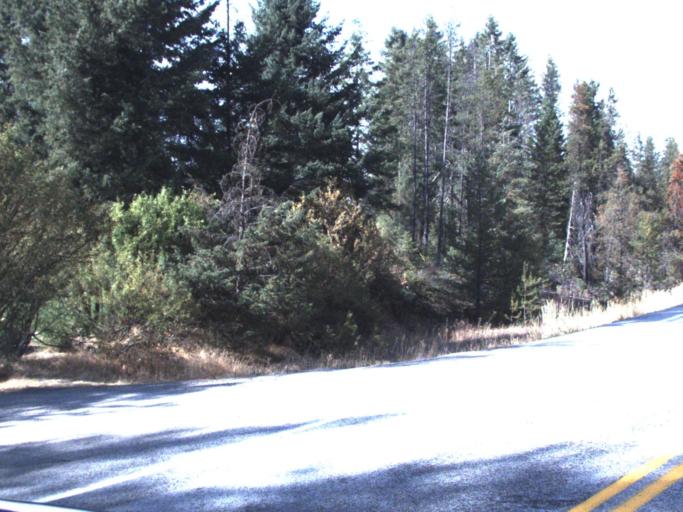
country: US
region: Washington
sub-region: Pend Oreille County
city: Newport
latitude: 48.1204
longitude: -117.2729
